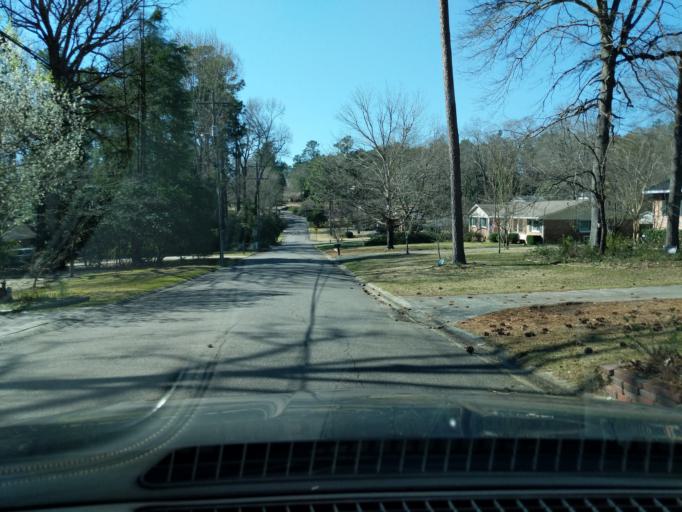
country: US
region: South Carolina
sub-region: Aiken County
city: Aiken
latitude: 33.5301
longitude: -81.7333
